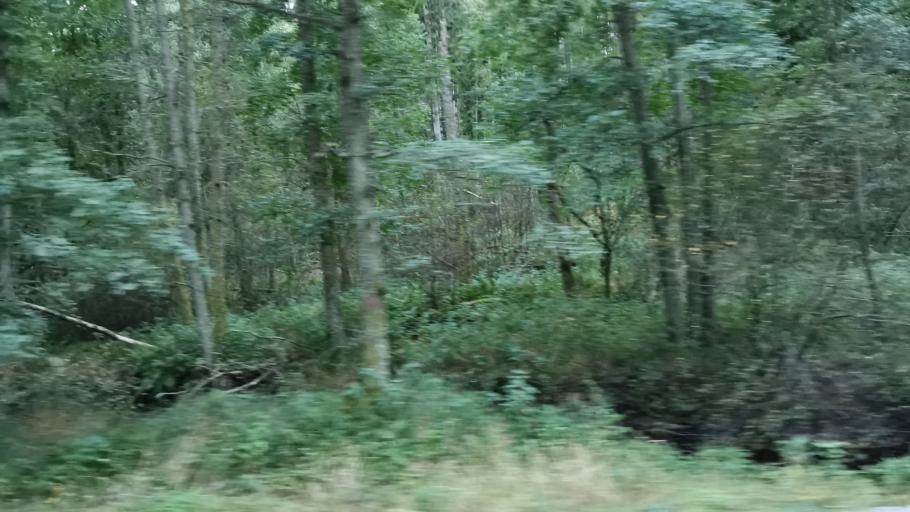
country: SE
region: Vaestra Goetaland
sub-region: Tanums Kommun
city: Tanumshede
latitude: 58.7045
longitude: 11.3366
